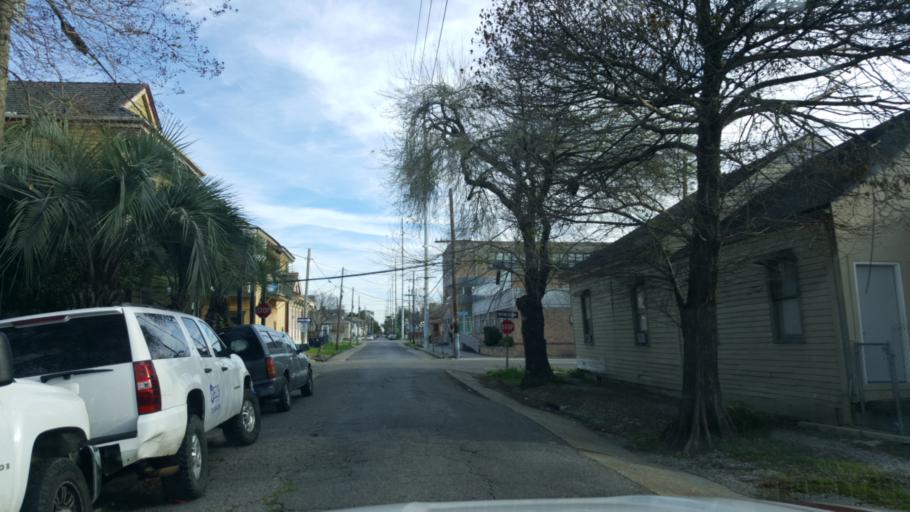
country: US
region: Louisiana
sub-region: Orleans Parish
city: New Orleans
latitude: 29.9679
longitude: -90.0743
